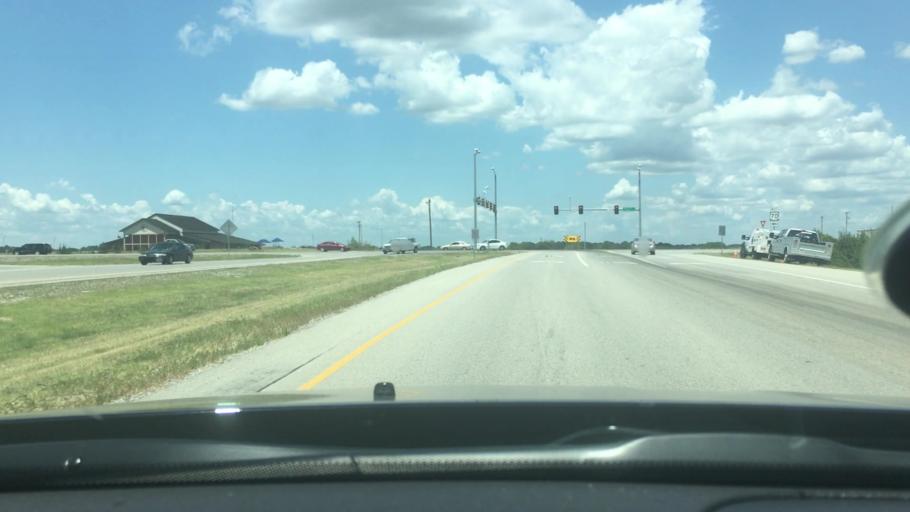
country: US
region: Oklahoma
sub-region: Bryan County
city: Durant
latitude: 33.9966
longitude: -96.4289
